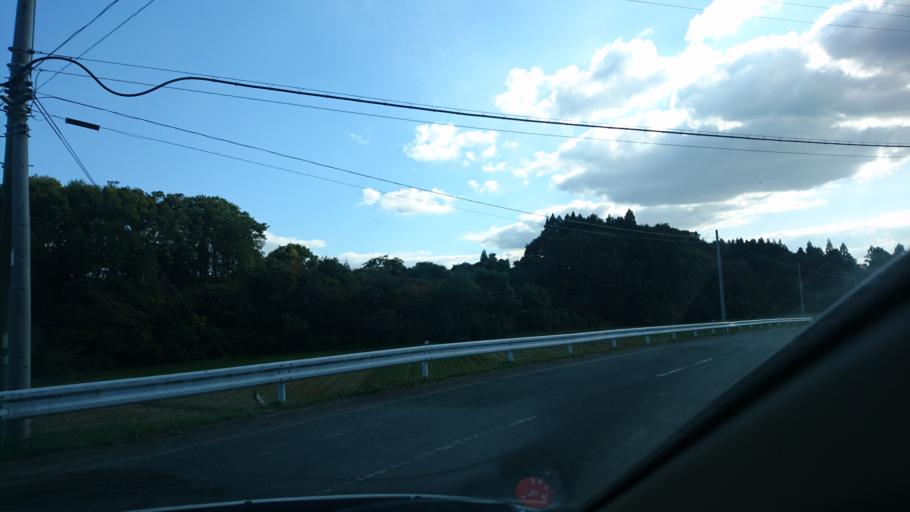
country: JP
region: Iwate
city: Kitakami
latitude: 39.2479
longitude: 141.1302
